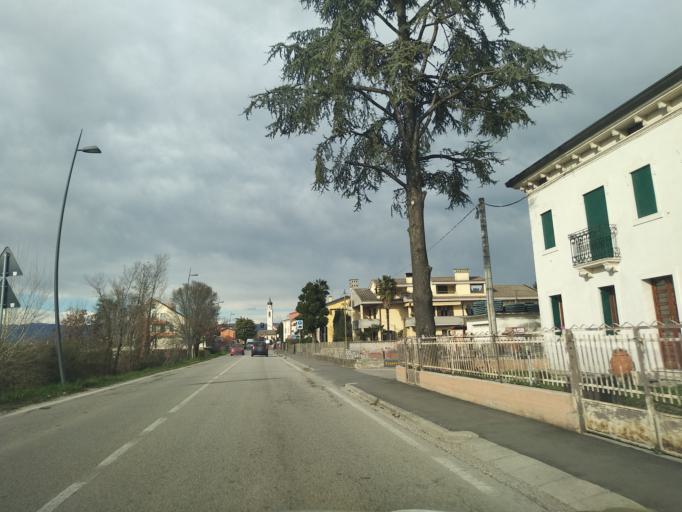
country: IT
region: Veneto
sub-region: Provincia di Vicenza
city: Bolzano Vicentino
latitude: 45.5992
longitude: 11.6216
